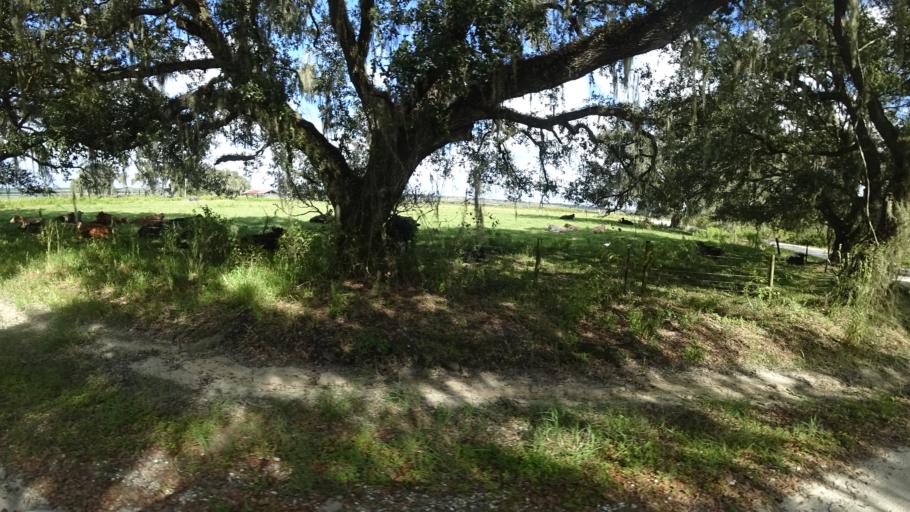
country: US
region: Florida
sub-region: Sarasota County
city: Lake Sarasota
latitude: 27.3240
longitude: -82.2197
